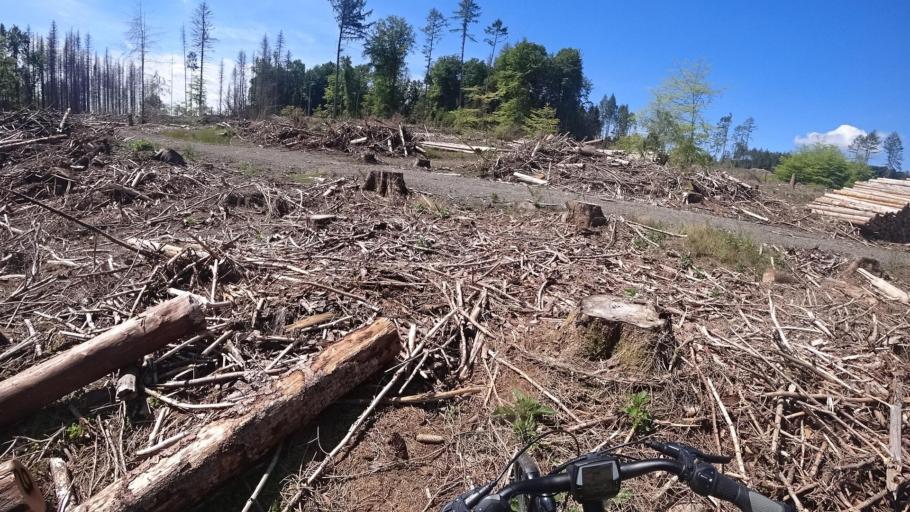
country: DE
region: Rheinland-Pfalz
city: Sorth
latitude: 50.7045
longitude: 7.6947
